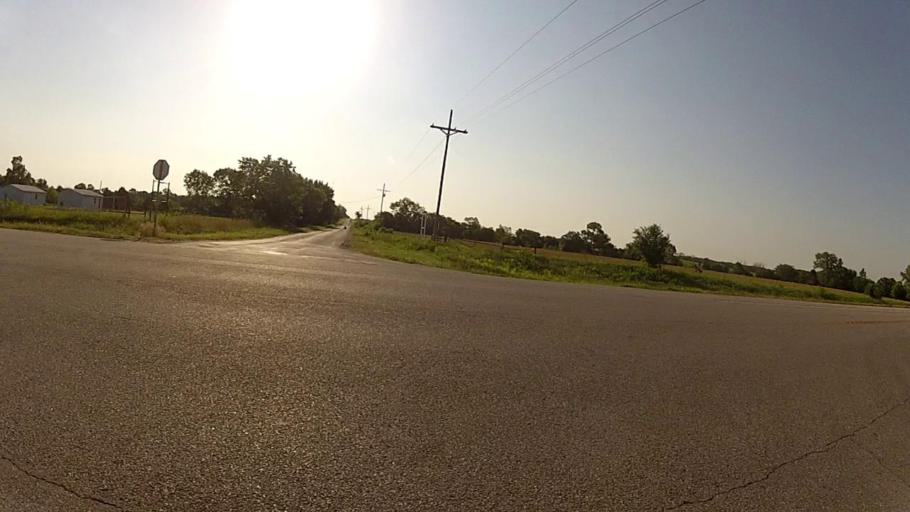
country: US
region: Kansas
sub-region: Montgomery County
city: Caney
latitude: 37.0963
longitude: -95.9288
